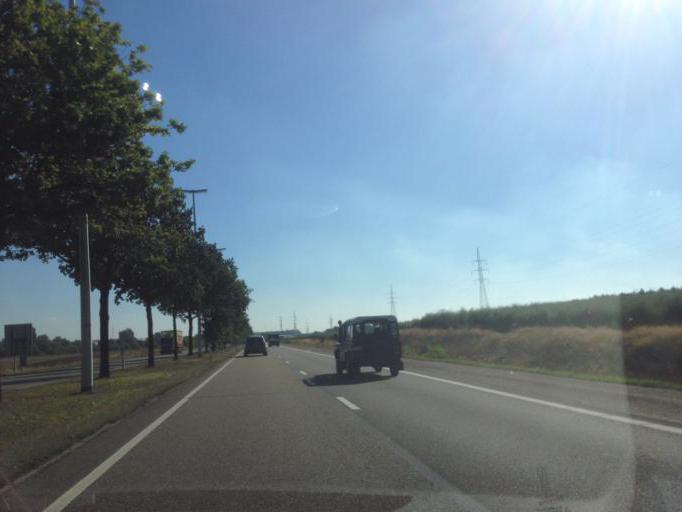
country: BE
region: Flanders
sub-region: Provincie Limburg
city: Overpelt
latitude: 51.2147
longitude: 5.3646
